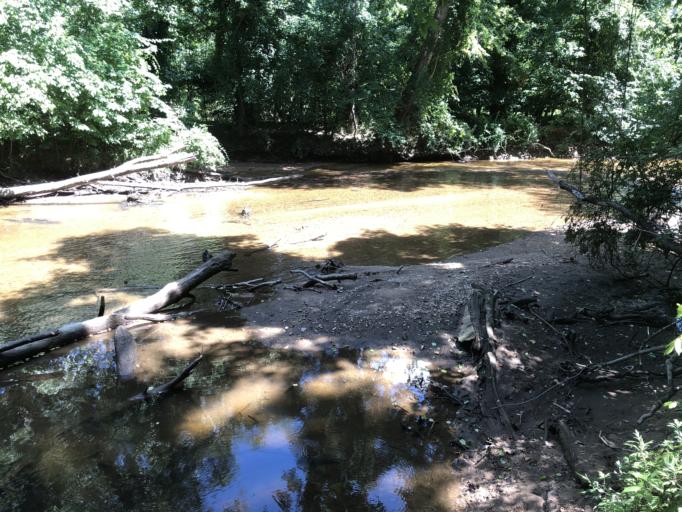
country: US
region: Virginia
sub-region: Fairfax County
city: Fort Belvoir
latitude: 38.7023
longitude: -77.1610
